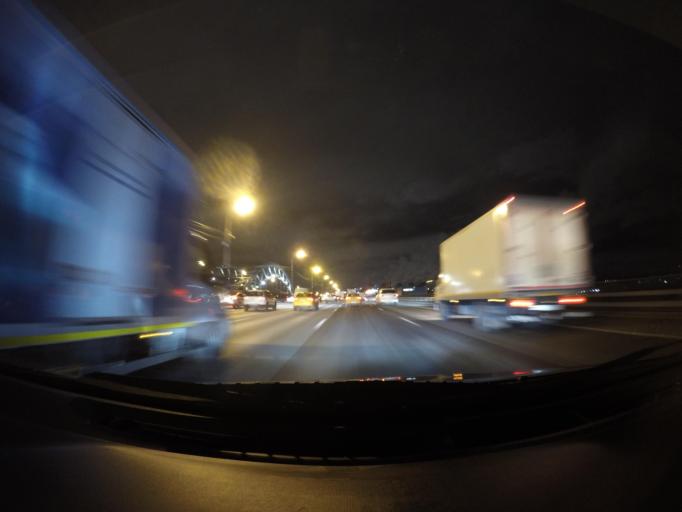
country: RU
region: Moskovskaya
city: Alekseyevka
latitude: 55.6225
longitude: 37.7921
